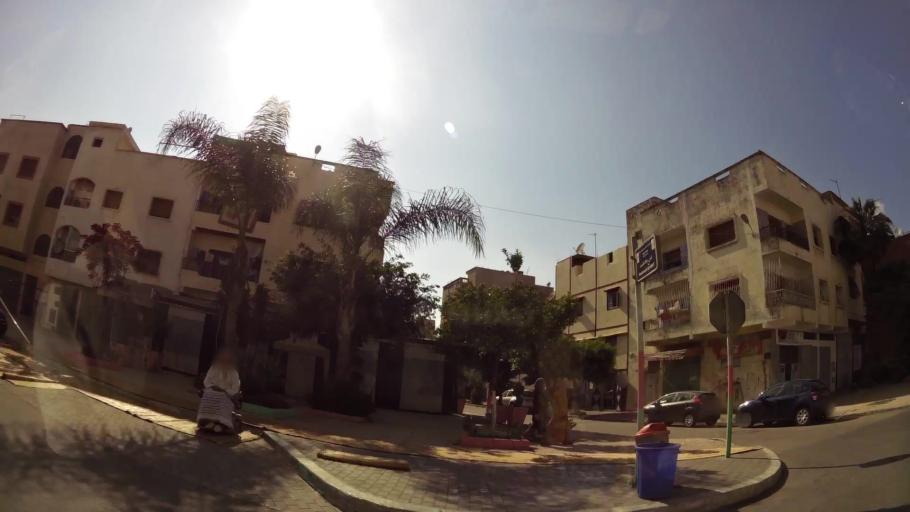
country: MA
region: Rabat-Sale-Zemmour-Zaer
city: Sale
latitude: 34.0415
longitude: -6.7799
